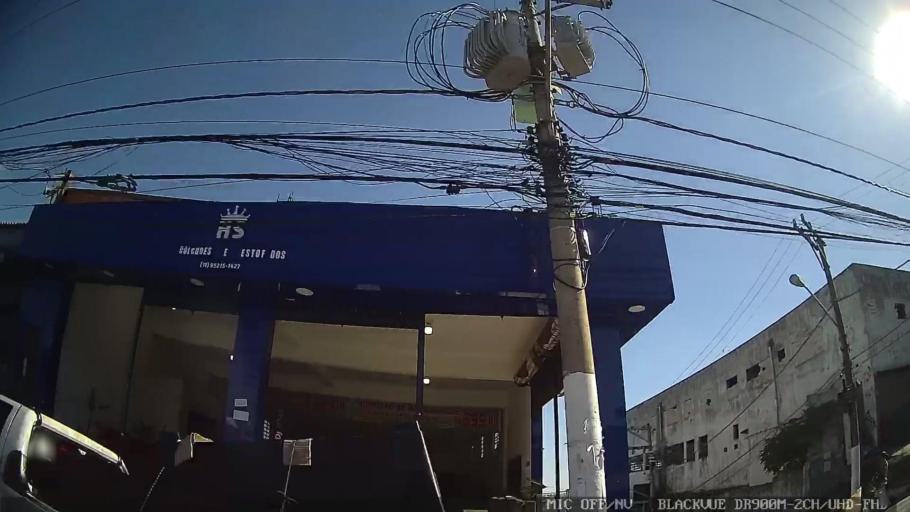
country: BR
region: Sao Paulo
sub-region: Guarulhos
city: Guarulhos
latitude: -23.5443
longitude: -46.4885
